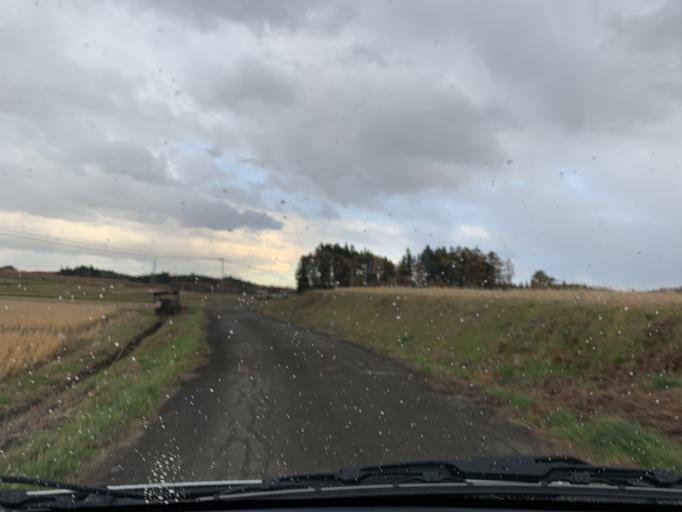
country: JP
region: Iwate
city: Mizusawa
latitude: 39.0879
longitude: 141.0000
